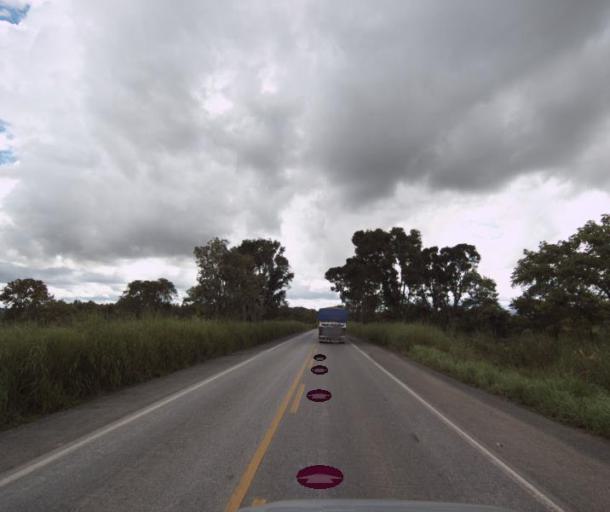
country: BR
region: Goias
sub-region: Uruacu
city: Uruacu
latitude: -14.2564
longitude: -49.1413
